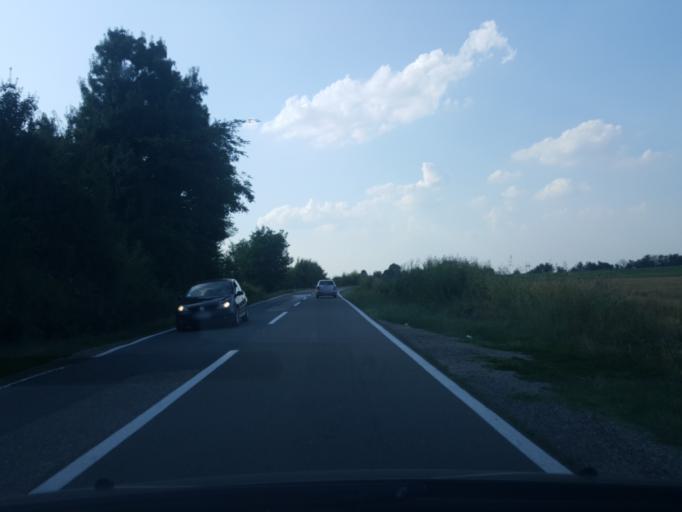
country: RS
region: Central Serbia
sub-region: Belgrade
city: Mladenovac
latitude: 44.3657
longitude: 20.6765
